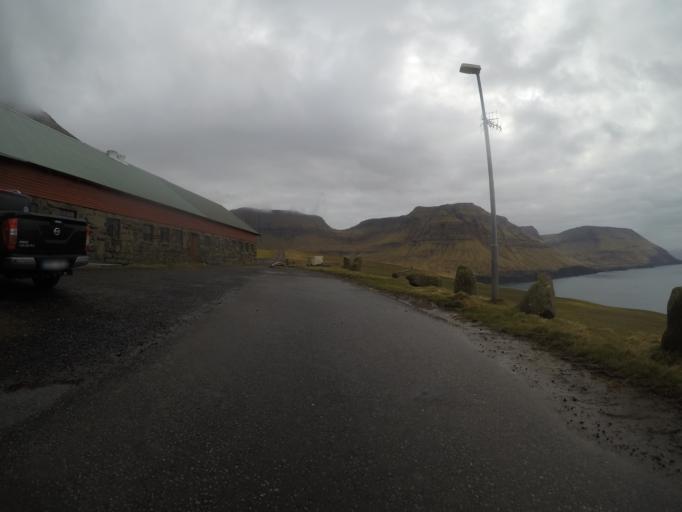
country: FO
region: Streymoy
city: Kollafjordhur
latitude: 62.0415
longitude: -6.9539
